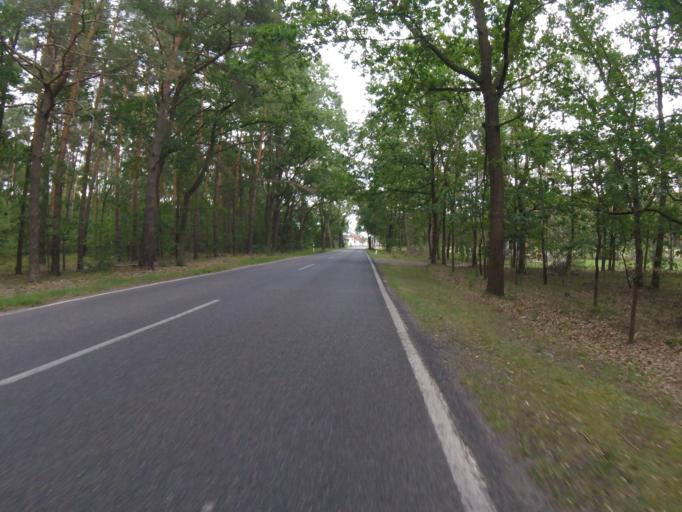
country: DE
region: Brandenburg
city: Halbe
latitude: 52.0945
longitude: 13.7143
